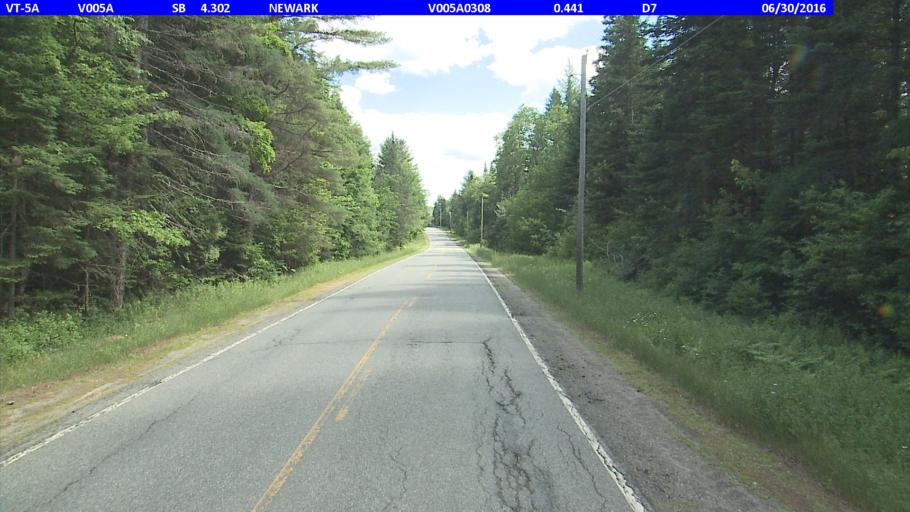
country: US
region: Vermont
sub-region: Caledonia County
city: Lyndonville
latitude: 44.6985
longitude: -72.0028
